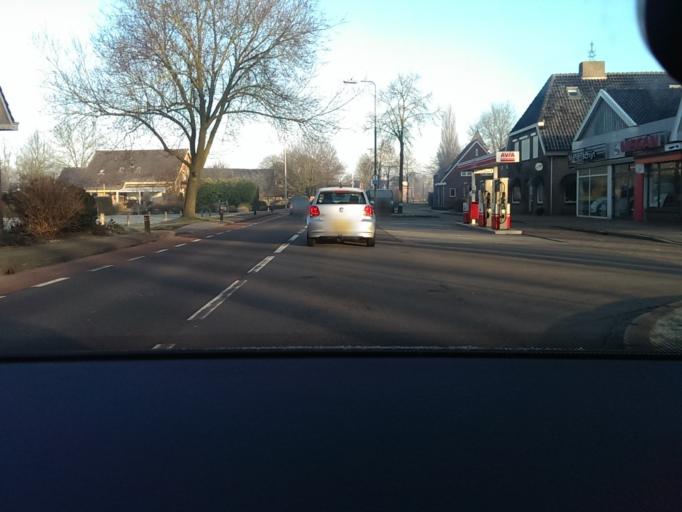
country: NL
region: Overijssel
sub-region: Gemeente Twenterand
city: Vroomshoop
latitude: 52.4305
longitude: 6.5406
